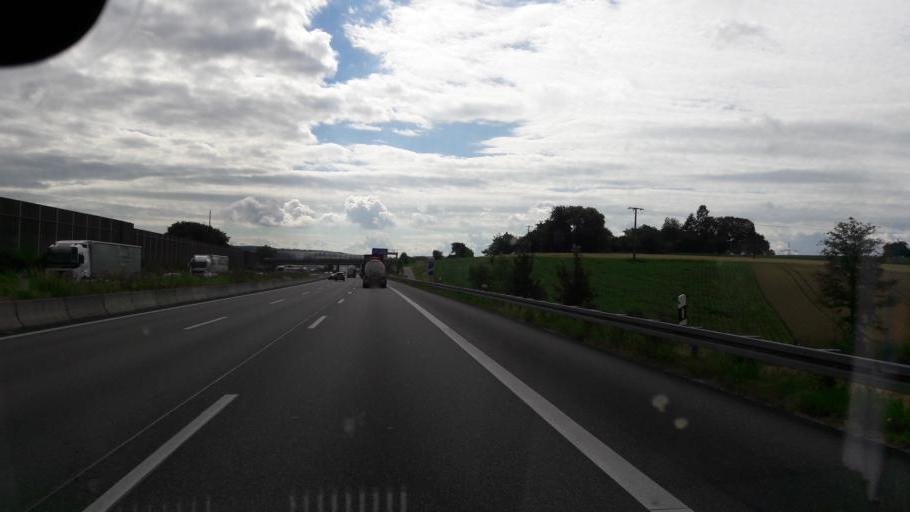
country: DE
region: Baden-Wuerttemberg
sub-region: Karlsruhe Region
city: Sinsheim
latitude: 49.2444
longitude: 8.8714
